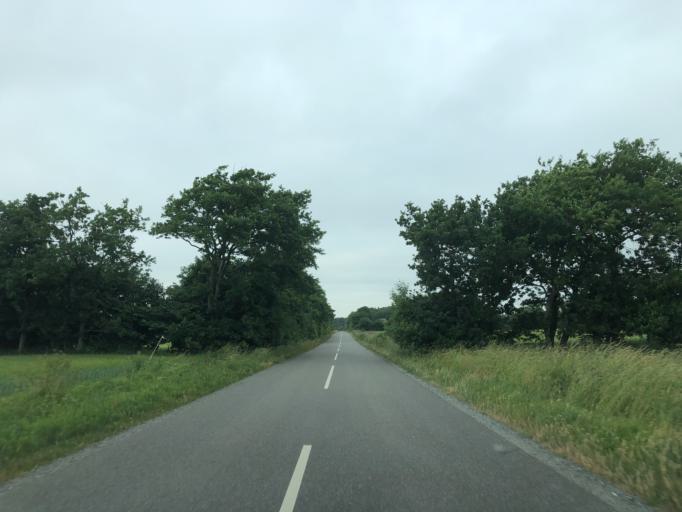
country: DK
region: Central Jutland
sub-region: Holstebro Kommune
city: Holstebro
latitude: 56.2446
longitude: 8.6232
